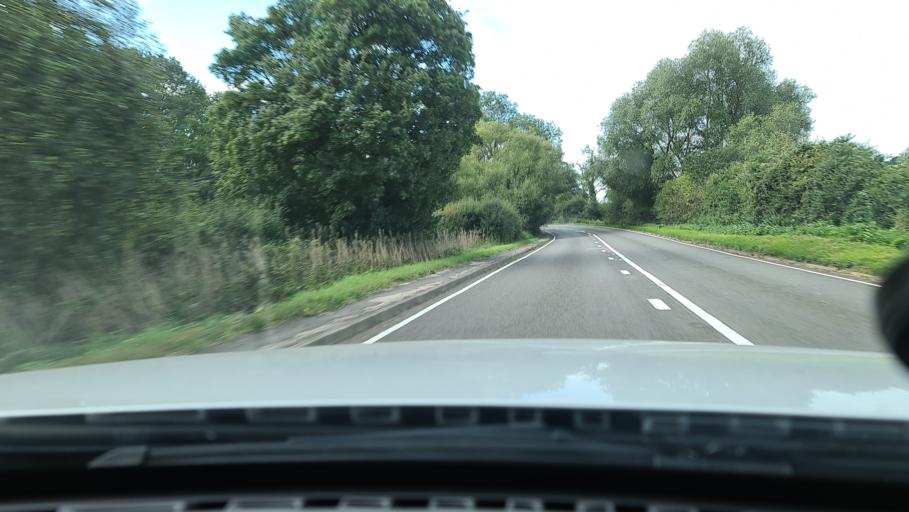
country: GB
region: England
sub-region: Warwickshire
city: Shipston on Stour
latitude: 52.0853
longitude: -1.6244
